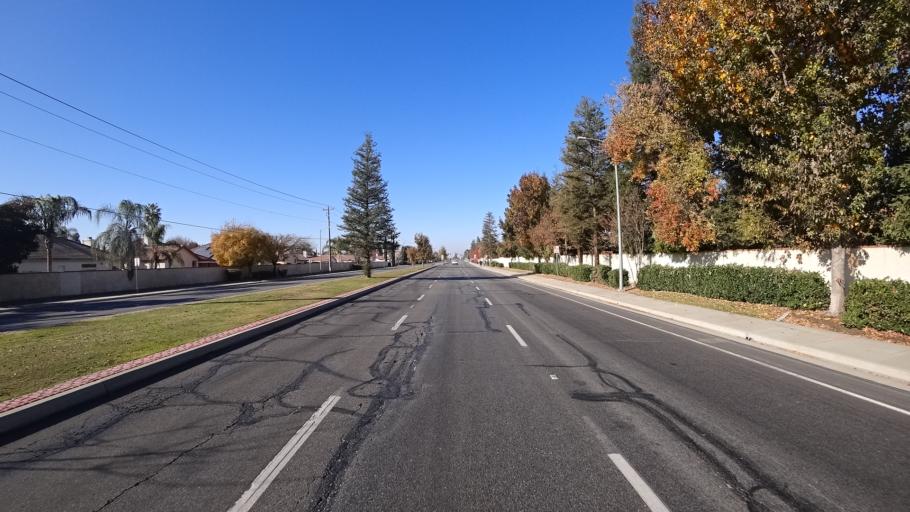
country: US
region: California
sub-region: Kern County
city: Greenacres
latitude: 35.3253
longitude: -119.1201
